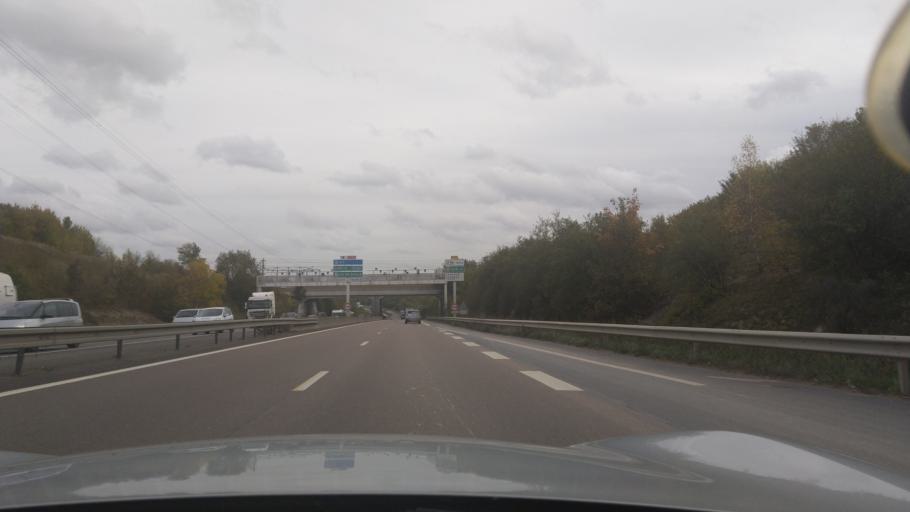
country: FR
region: Ile-de-France
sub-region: Departement du Val-d'Oise
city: Louvres
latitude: 49.0391
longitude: 2.4842
